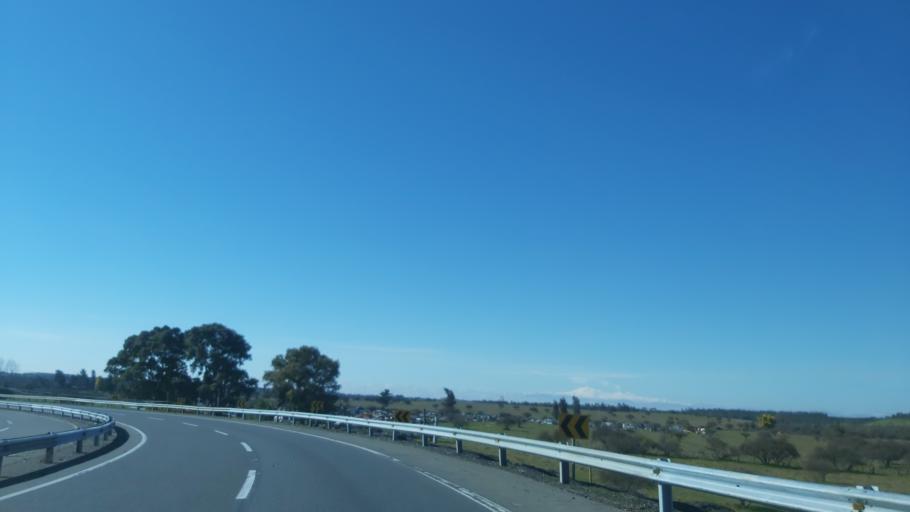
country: CL
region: Biobio
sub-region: Provincia de Nuble
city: Bulnes
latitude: -36.6564
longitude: -72.2288
